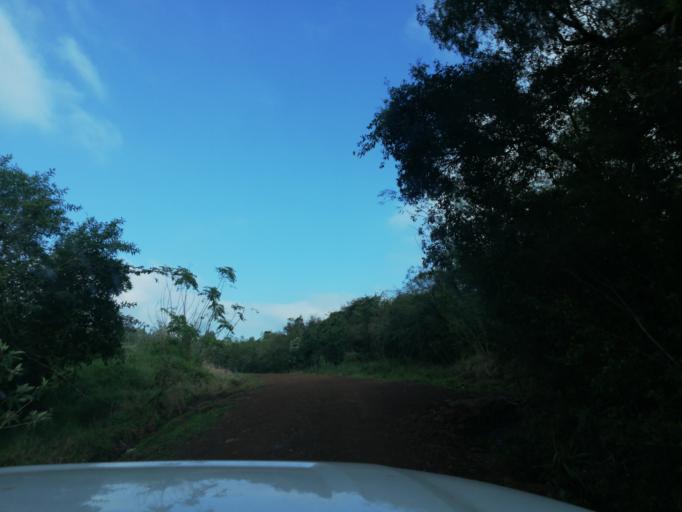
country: AR
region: Misiones
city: Cerro Azul
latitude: -27.5752
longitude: -55.5052
